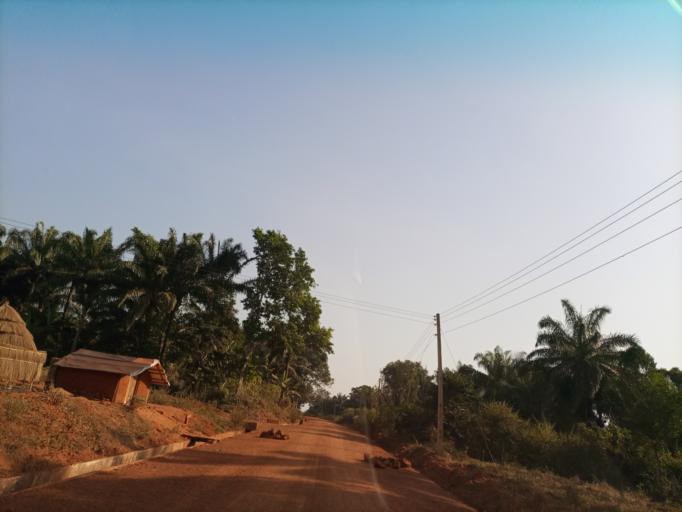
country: NG
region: Enugu
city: Opi
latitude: 6.7724
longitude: 7.3910
